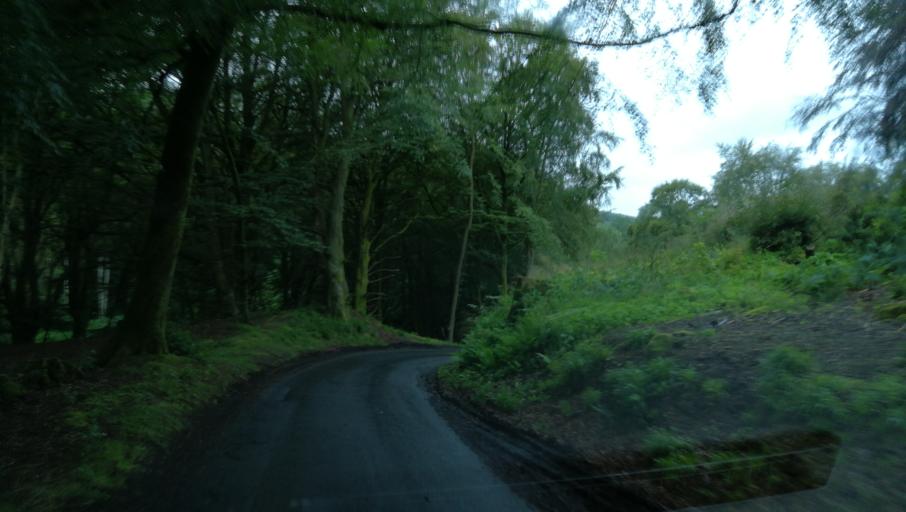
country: GB
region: Scotland
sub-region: Perth and Kinross
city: Alyth
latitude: 56.6255
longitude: -3.2587
